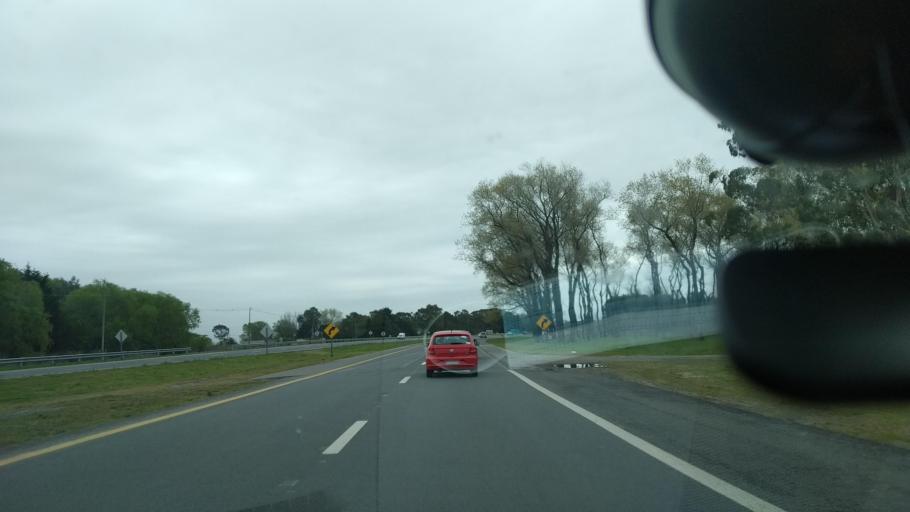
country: AR
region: Buenos Aires
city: Mar del Tuyu
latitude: -36.4859
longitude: -56.7129
